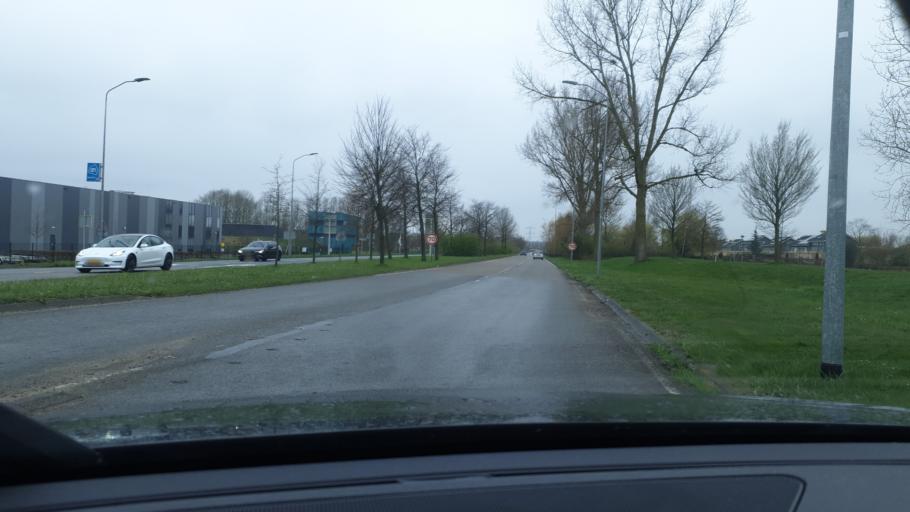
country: NL
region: Flevoland
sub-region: Gemeente Lelystad
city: Lelystad
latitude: 52.4992
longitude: 5.5101
